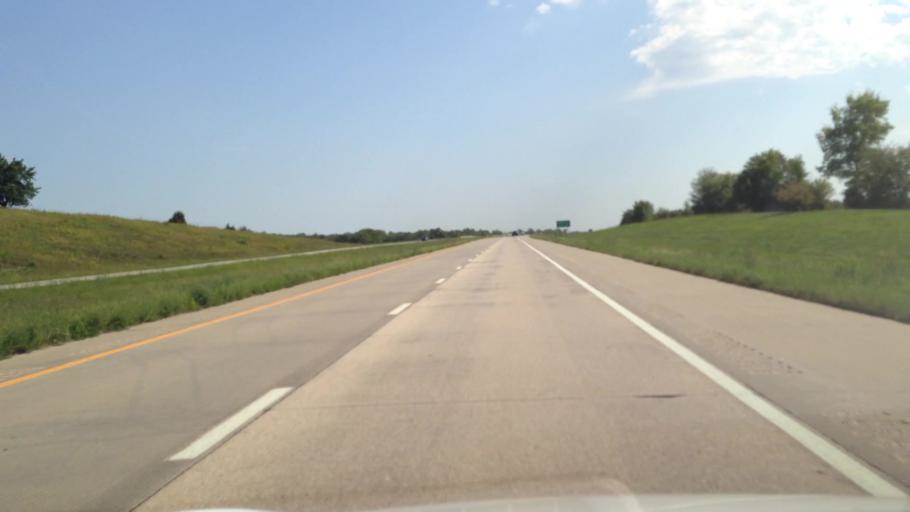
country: US
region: Kansas
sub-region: Miami County
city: Louisburg
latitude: 38.5386
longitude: -94.6848
